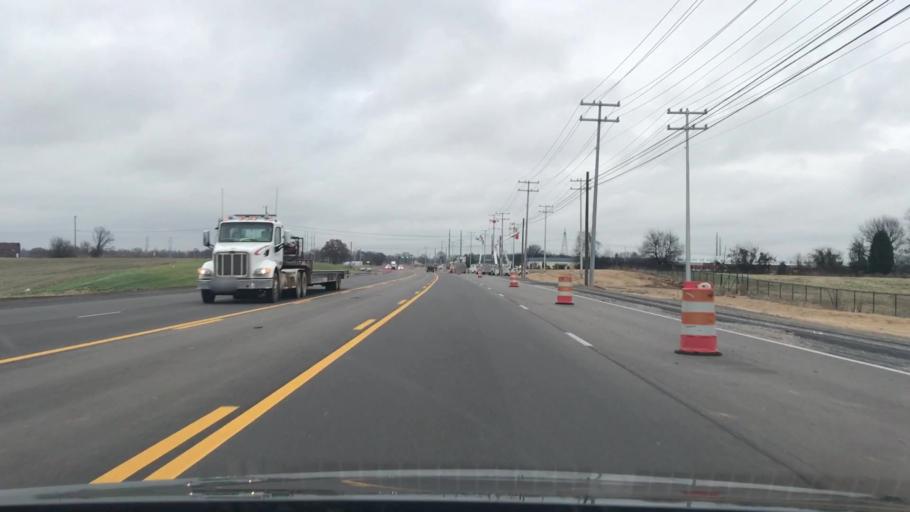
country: US
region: Kentucky
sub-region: Todd County
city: Guthrie
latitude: 36.6090
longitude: -87.2636
